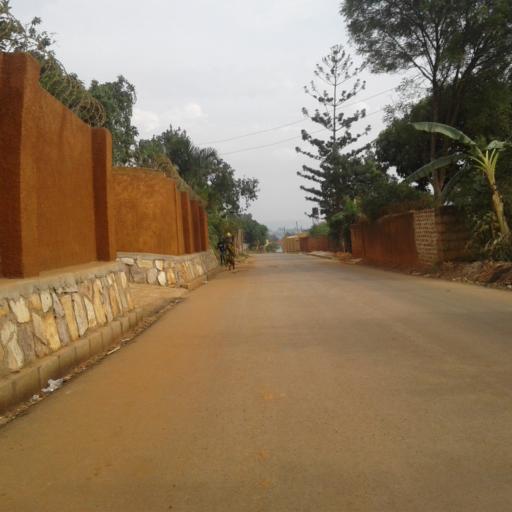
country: UG
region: Central Region
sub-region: Kampala District
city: Kampala
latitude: 0.2715
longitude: 32.6268
